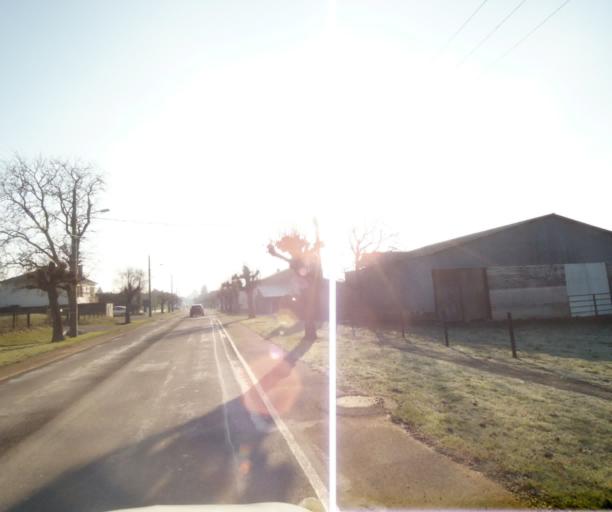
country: FR
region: Champagne-Ardenne
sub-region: Departement de la Haute-Marne
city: Montier-en-Der
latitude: 48.4832
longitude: 4.7633
